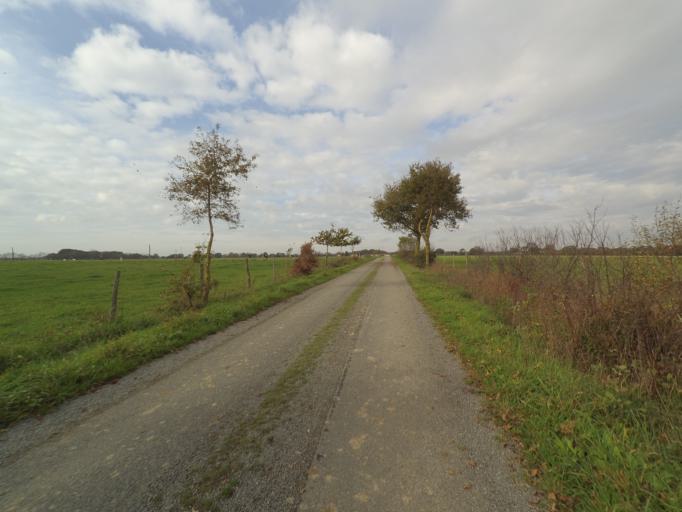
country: FR
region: Pays de la Loire
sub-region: Departement de la Loire-Atlantique
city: Vieillevigne
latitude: 46.9915
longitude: -1.3972
